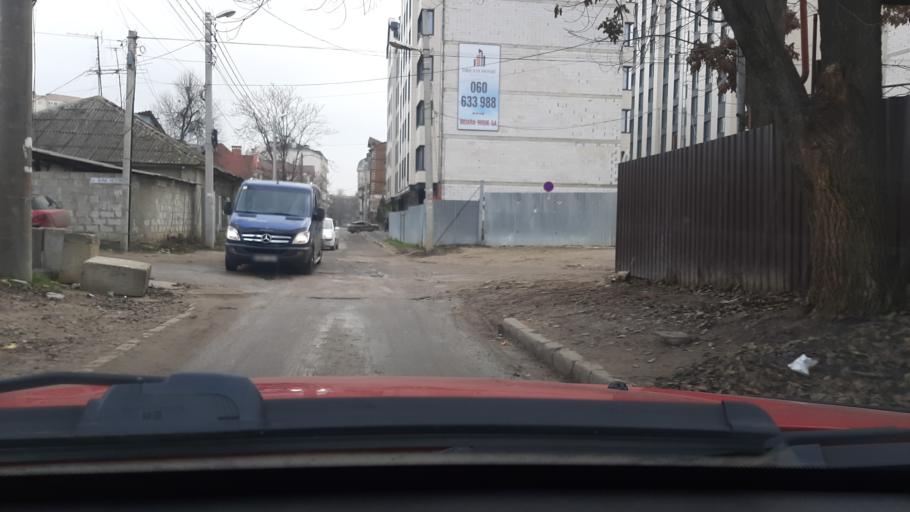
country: MD
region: Chisinau
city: Chisinau
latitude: 47.0356
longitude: 28.8372
